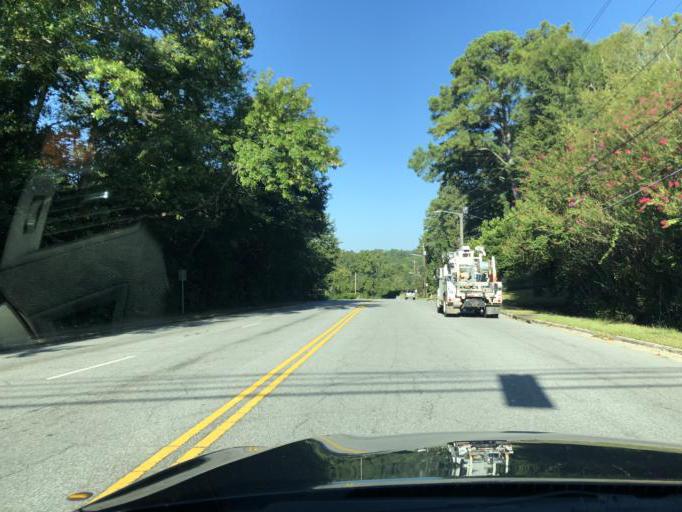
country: US
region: Georgia
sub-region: Muscogee County
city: Columbus
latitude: 32.4908
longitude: -84.9375
